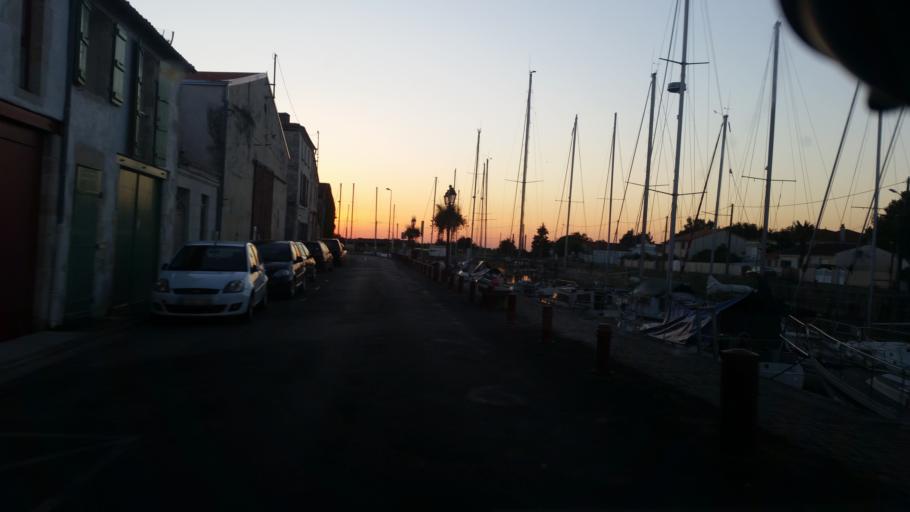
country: FR
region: Poitou-Charentes
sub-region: Departement de la Charente-Maritime
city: Marans
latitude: 46.3123
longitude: -0.9957
